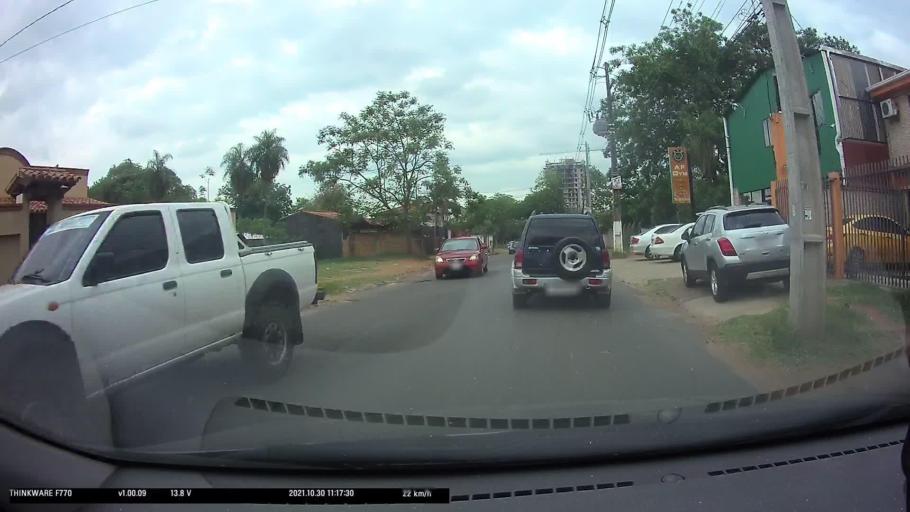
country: PY
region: Central
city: Fernando de la Mora
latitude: -25.3153
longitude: -57.5181
